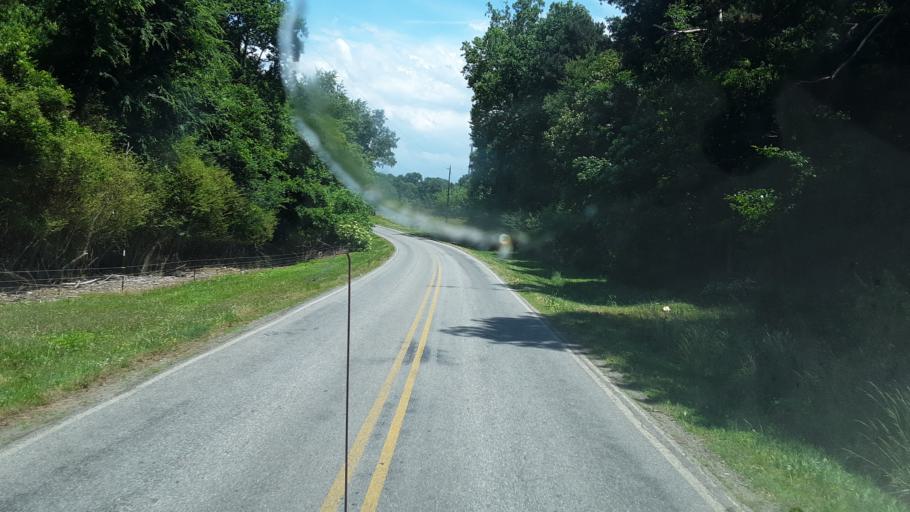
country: US
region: North Carolina
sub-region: Yadkin County
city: Jonesville
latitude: 36.0691
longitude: -80.8311
